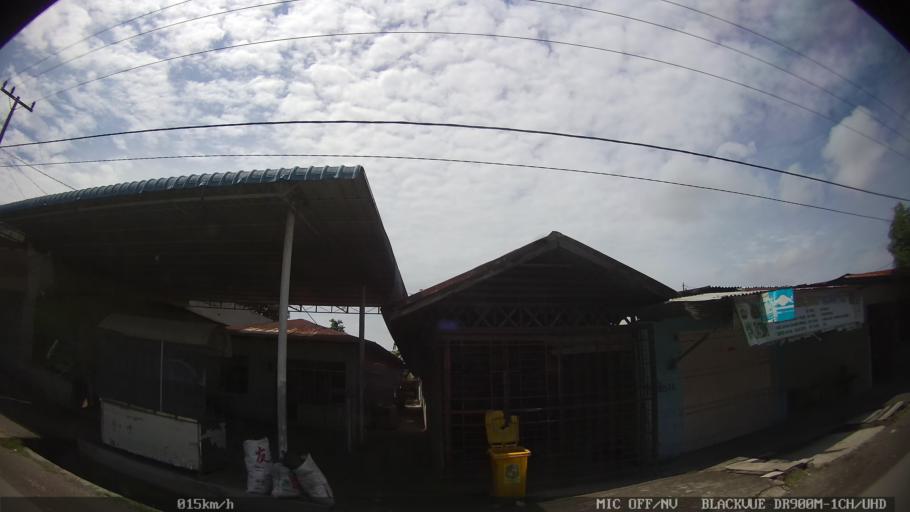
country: ID
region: North Sumatra
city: Medan
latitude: 3.5910
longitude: 98.7544
